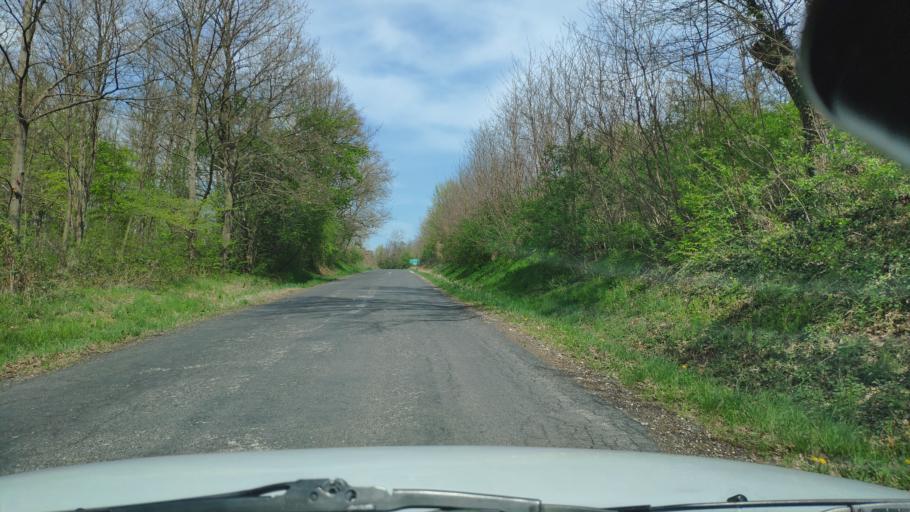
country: HU
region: Zala
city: Nagykanizsa
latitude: 46.4197
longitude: 17.0404
